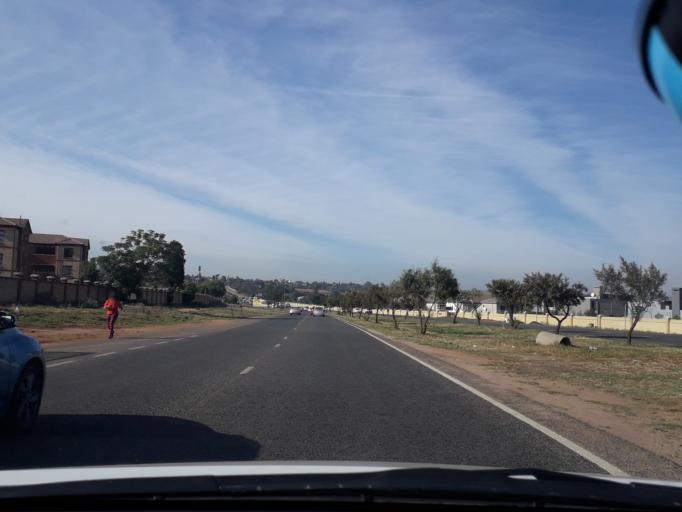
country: ZA
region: Gauteng
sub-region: City of Johannesburg Metropolitan Municipality
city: Roodepoort
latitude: -26.0904
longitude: 27.9277
